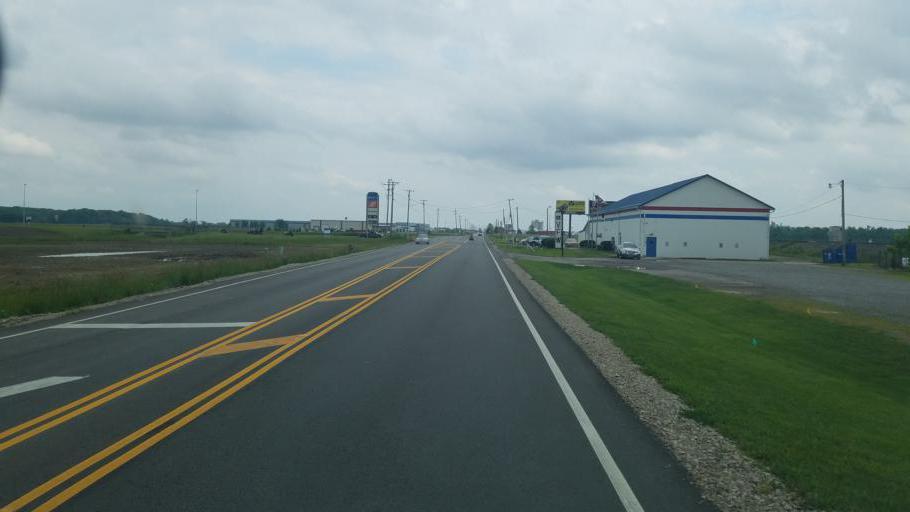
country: US
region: Ohio
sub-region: Union County
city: Marysville
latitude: 40.2255
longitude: -83.3414
